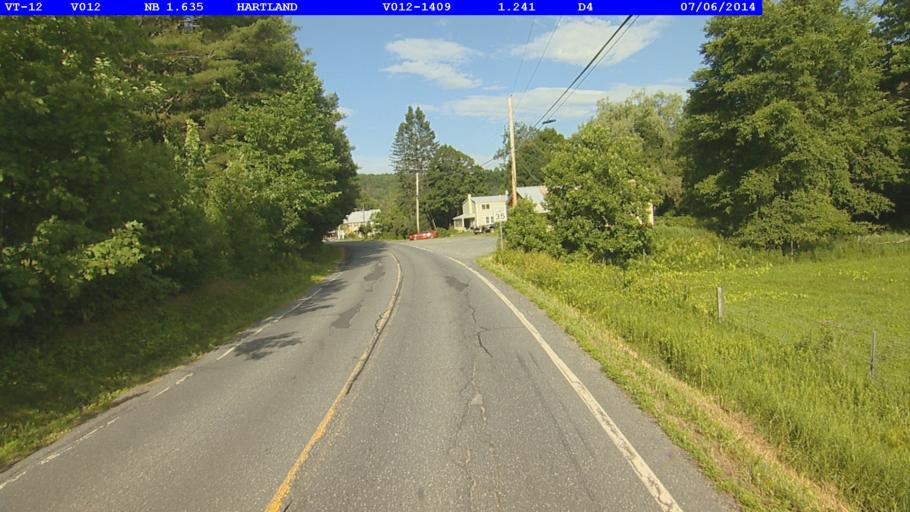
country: US
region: Vermont
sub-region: Windsor County
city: Windsor
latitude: 43.5474
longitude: -72.4208
